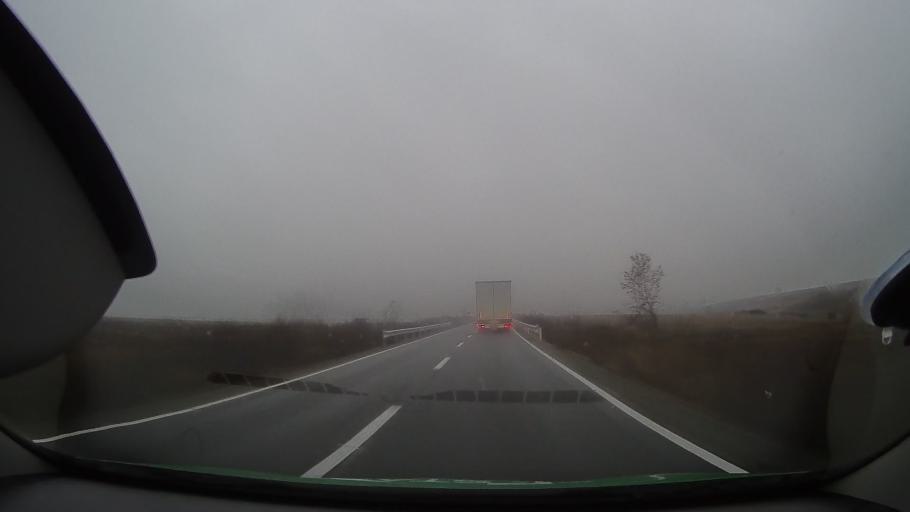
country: RO
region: Bihor
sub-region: Comuna Olcea
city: Olcea
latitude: 46.6644
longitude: 21.9631
